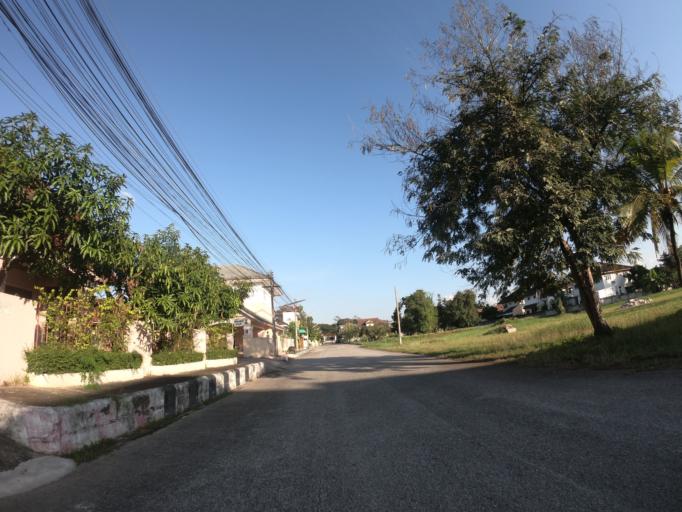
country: TH
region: Chiang Mai
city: Chiang Mai
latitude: 18.7402
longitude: 98.9759
